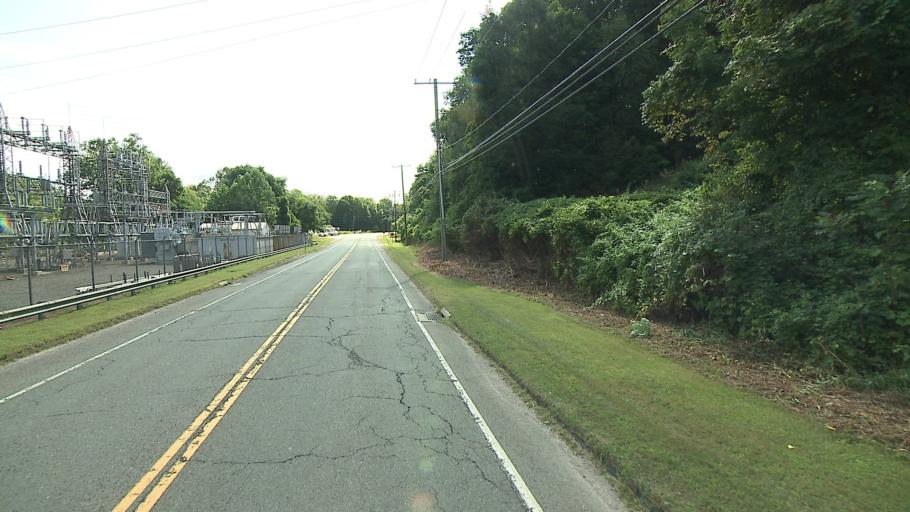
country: US
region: Connecticut
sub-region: Litchfield County
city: New Milford
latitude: 41.5823
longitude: -73.4343
